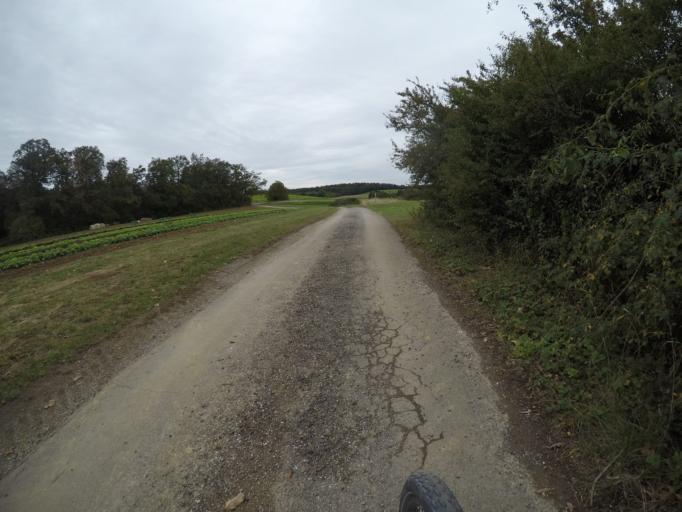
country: DE
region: Baden-Wuerttemberg
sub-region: Regierungsbezirk Stuttgart
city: Eberdingen
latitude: 48.8836
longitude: 8.9801
